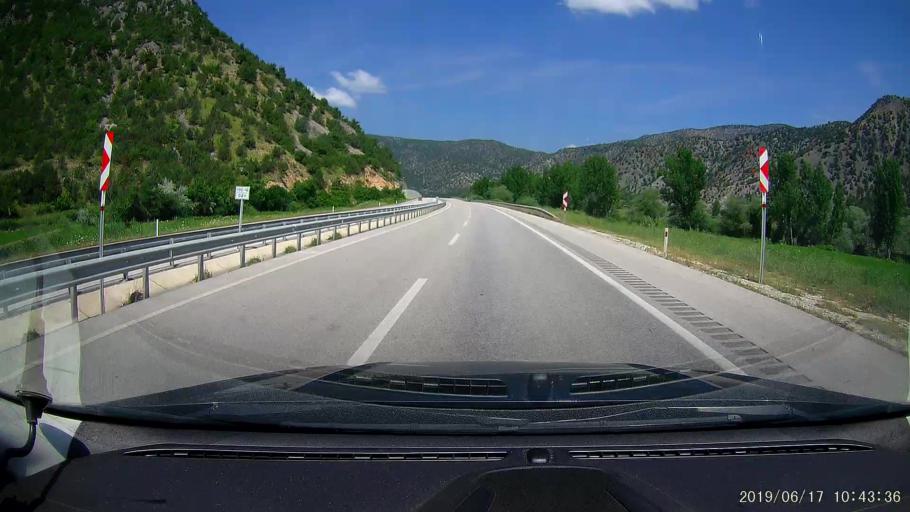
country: TR
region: Corum
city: Kargi
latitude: 41.0668
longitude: 34.5324
